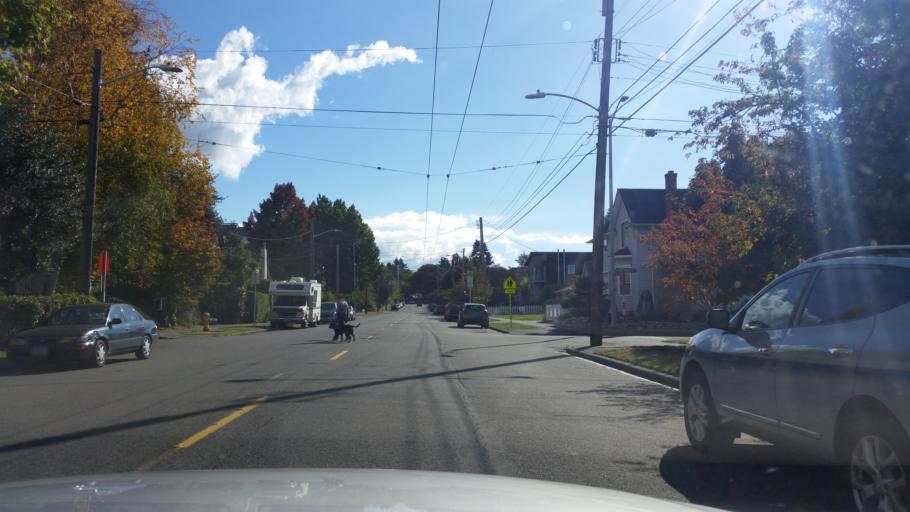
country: US
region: Washington
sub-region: King County
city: Seattle
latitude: 47.6423
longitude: -122.3663
